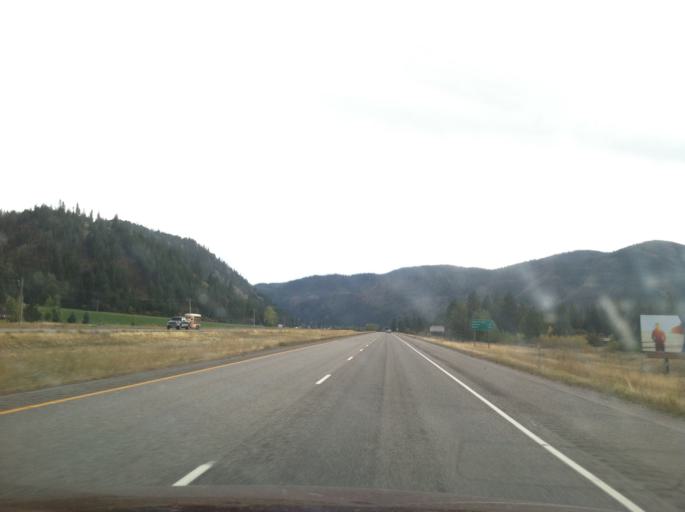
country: US
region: Montana
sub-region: Missoula County
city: Clinton
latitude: 46.7733
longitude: -113.7112
